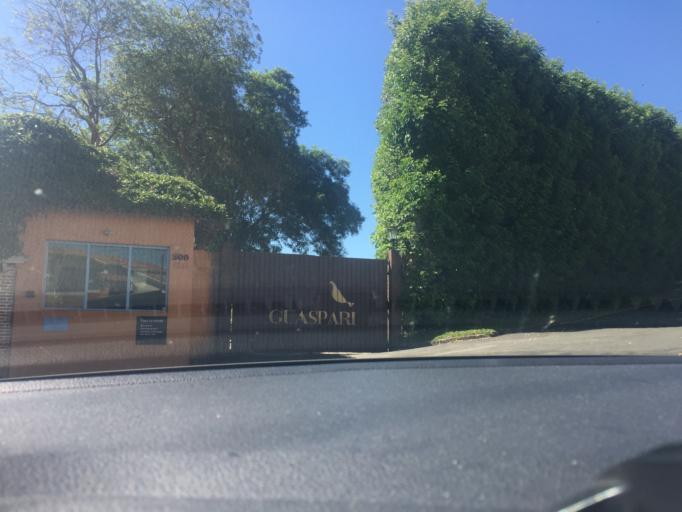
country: BR
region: Sao Paulo
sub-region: Santo Antonio Do Jardim
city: Espirito Santo do Pinhal
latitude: -22.1804
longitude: -46.7419
